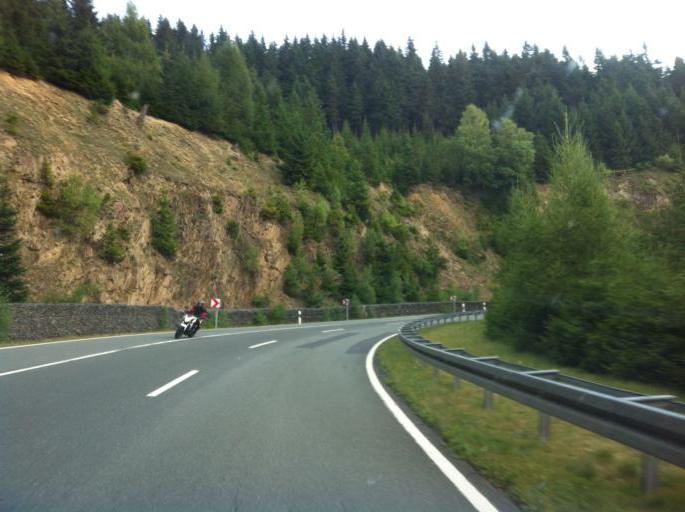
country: DE
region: Thuringia
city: Goldisthal
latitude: 50.5116
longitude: 11.0069
